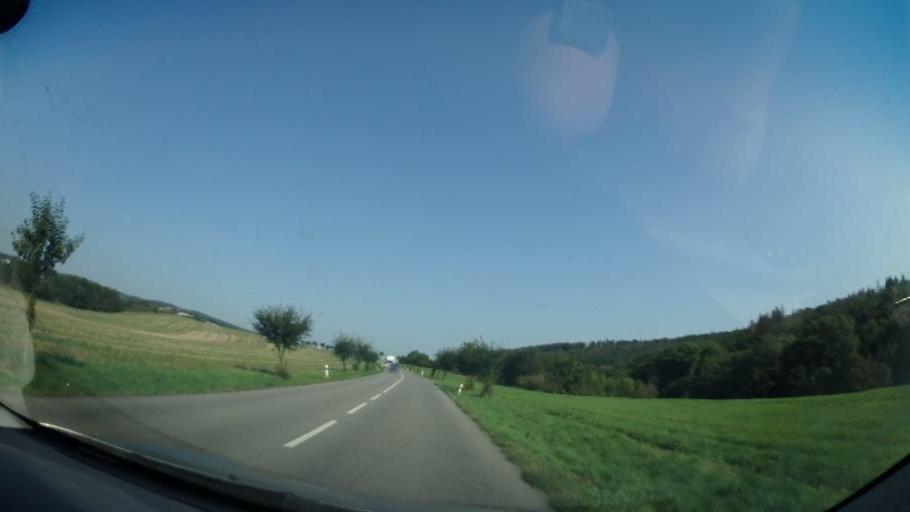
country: CZ
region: South Moravian
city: Kurim
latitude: 49.2442
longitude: 16.5300
